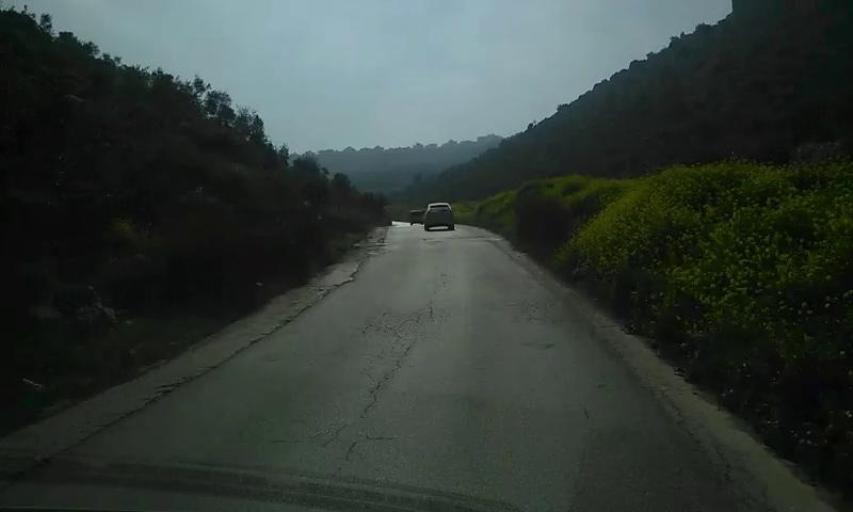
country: PS
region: West Bank
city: `Ayn Yabrud
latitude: 31.9526
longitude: 35.2394
